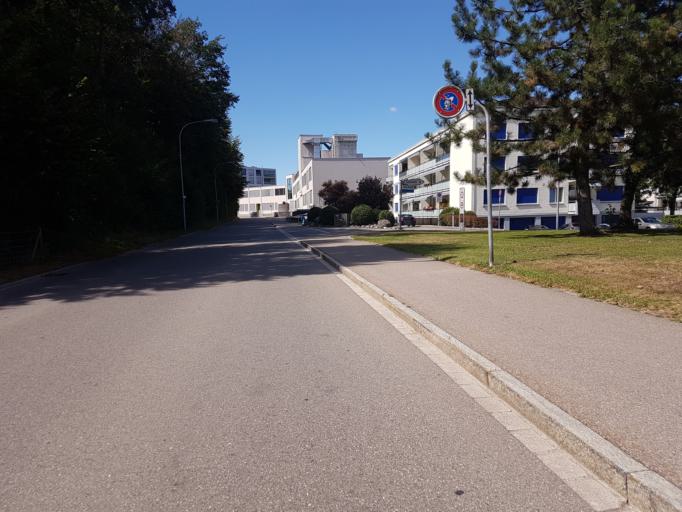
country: CH
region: Zurich
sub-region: Bezirk Pfaeffikon
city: Effretikon
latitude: 47.4228
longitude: 8.6900
